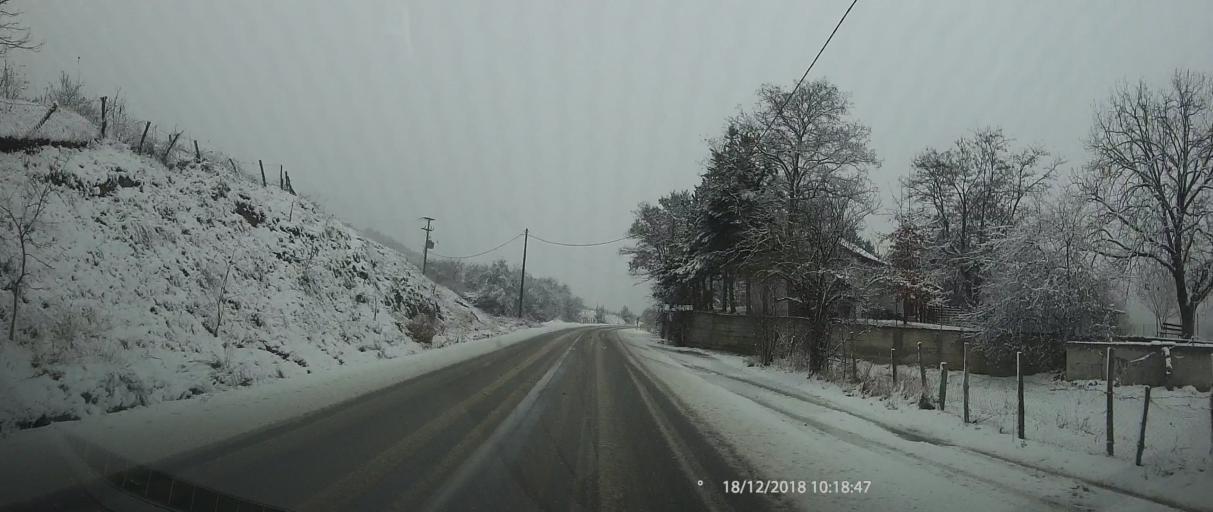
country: GR
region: Thessaly
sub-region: Nomos Larisis
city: Livadi
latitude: 40.1344
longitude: 22.2191
